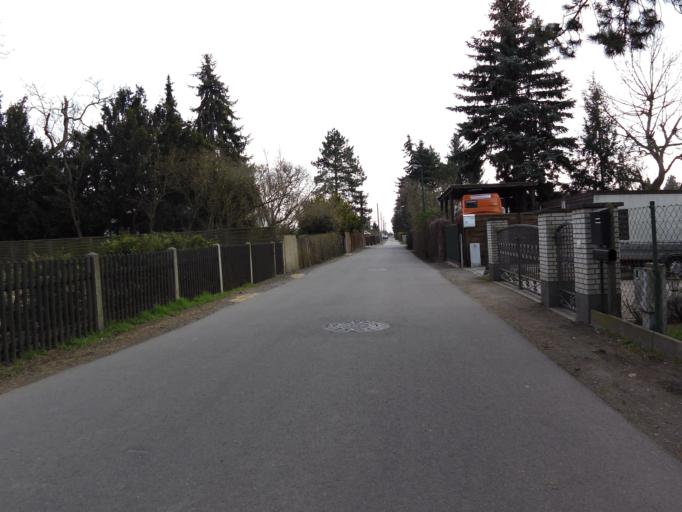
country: DE
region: Saxony
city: Markranstadt
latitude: 51.3103
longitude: 12.2820
